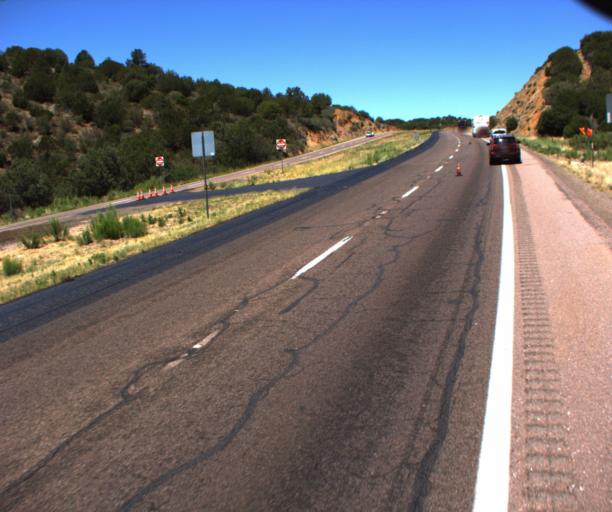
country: US
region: Arizona
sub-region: Gila County
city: Payson
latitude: 34.1639
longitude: -111.3273
